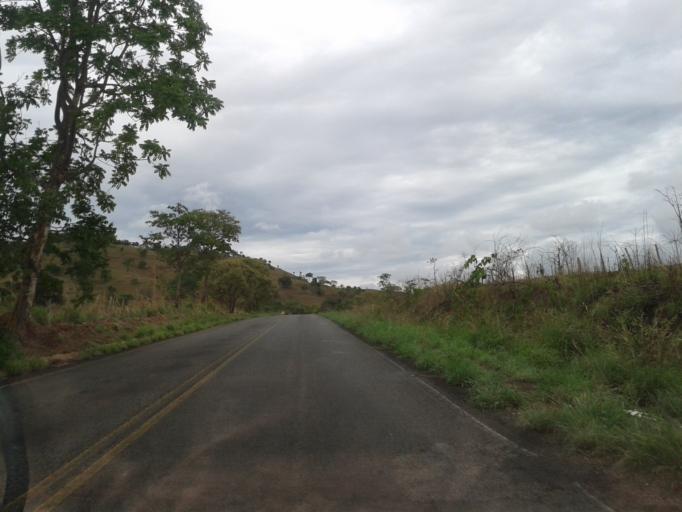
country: BR
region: Goias
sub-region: Caldas Novas
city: Caldas Novas
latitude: -18.0612
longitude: -48.6973
